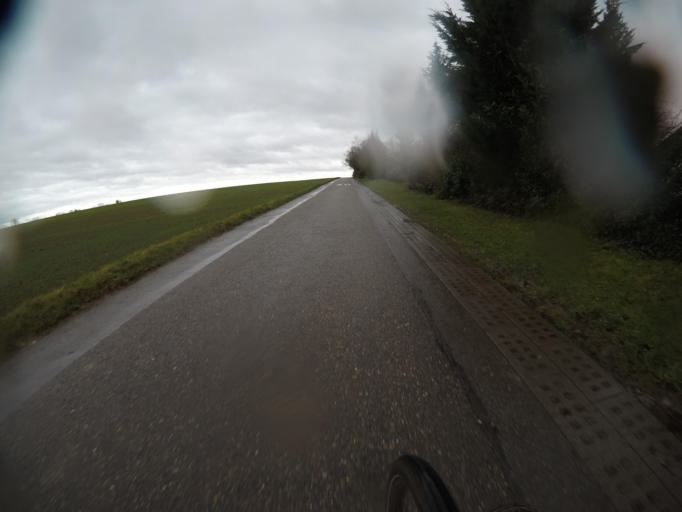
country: DE
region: Baden-Wuerttemberg
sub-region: Regierungsbezirk Stuttgart
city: Bietigheim-Bissingen
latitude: 48.9415
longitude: 9.1587
